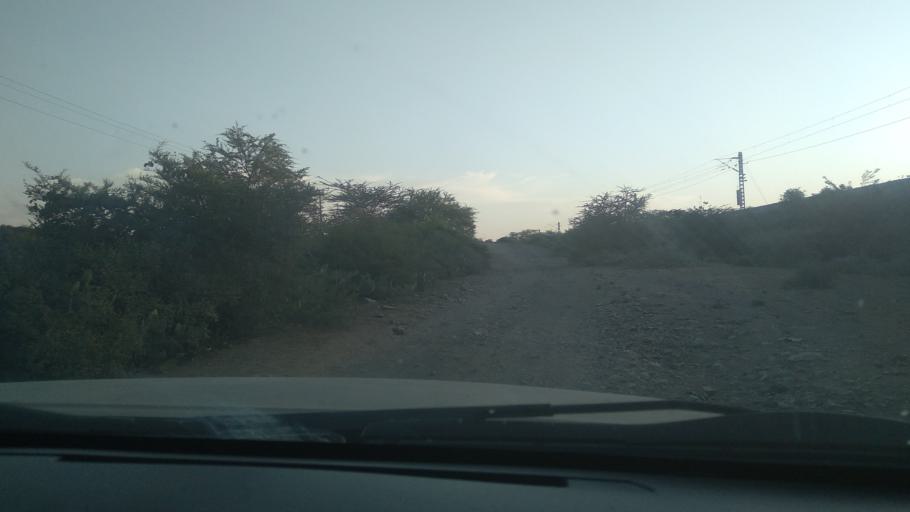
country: ET
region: Oromiya
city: Asbe Teferi
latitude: 9.2564
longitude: 40.7892
